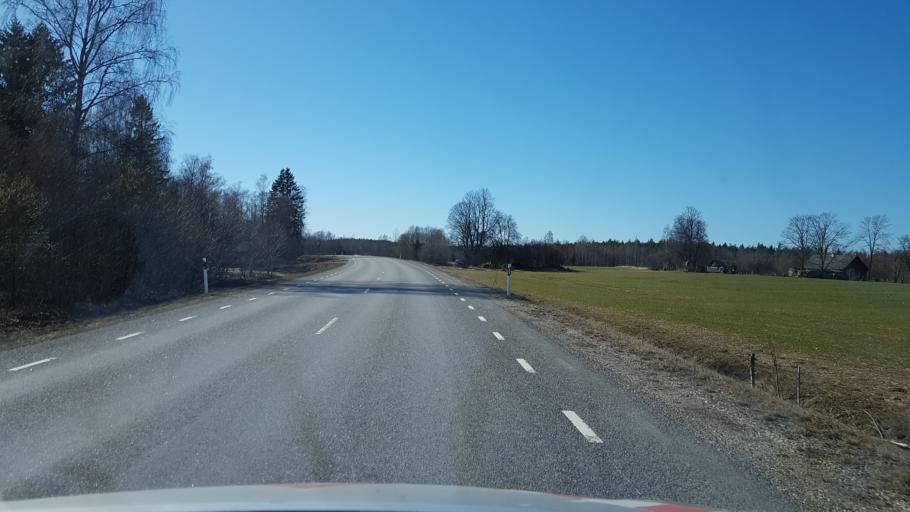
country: EE
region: Ida-Virumaa
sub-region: Aseri vald
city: Aseri
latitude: 59.3554
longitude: 26.7287
